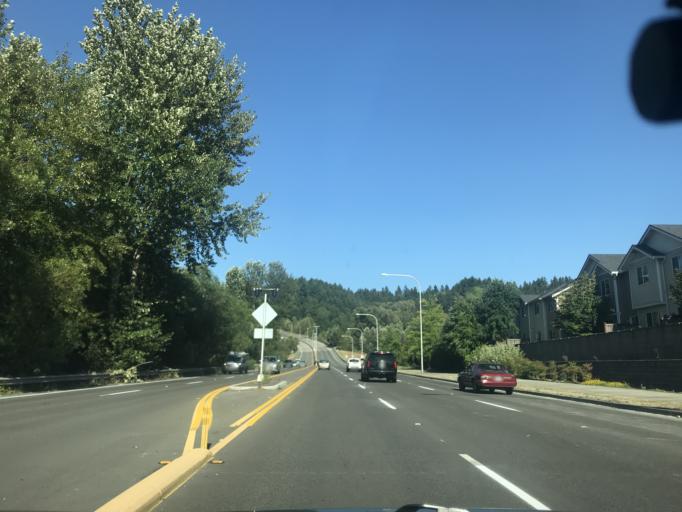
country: US
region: Washington
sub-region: King County
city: Kent
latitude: 47.3536
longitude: -122.2153
